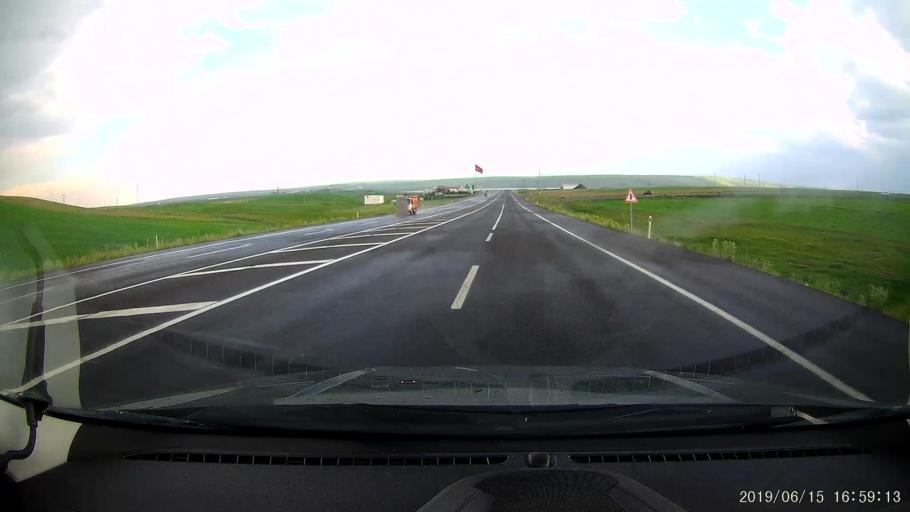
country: TR
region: Kars
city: Susuz
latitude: 40.7548
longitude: 43.1491
